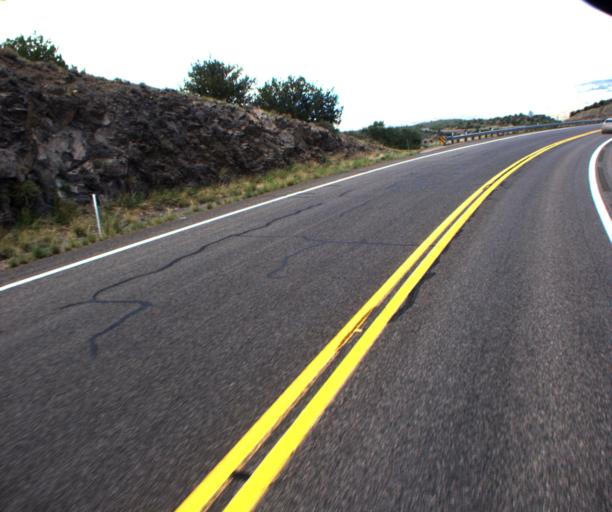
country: US
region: Arizona
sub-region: Yavapai County
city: Lake Montezuma
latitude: 34.4978
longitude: -111.7184
